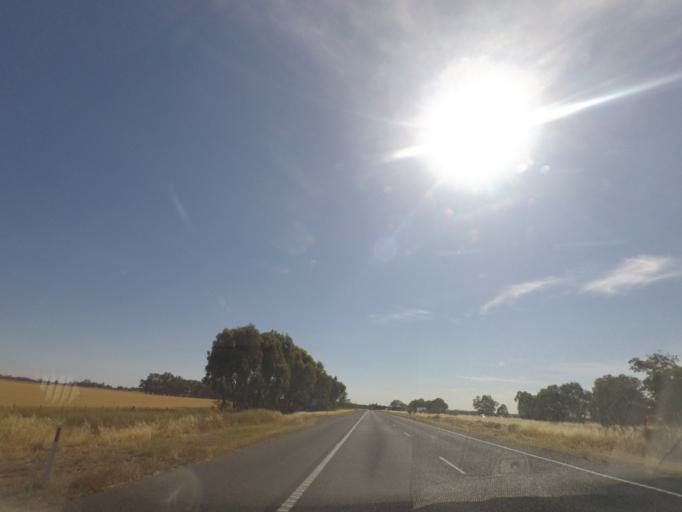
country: AU
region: Victoria
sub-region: Greater Shepparton
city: Shepparton
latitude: -36.6742
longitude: 145.2543
